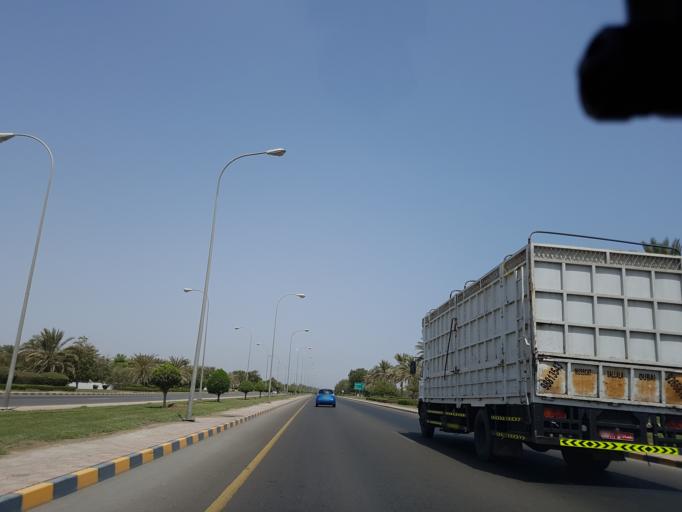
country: OM
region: Al Batinah
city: Saham
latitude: 24.2370
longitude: 56.8228
